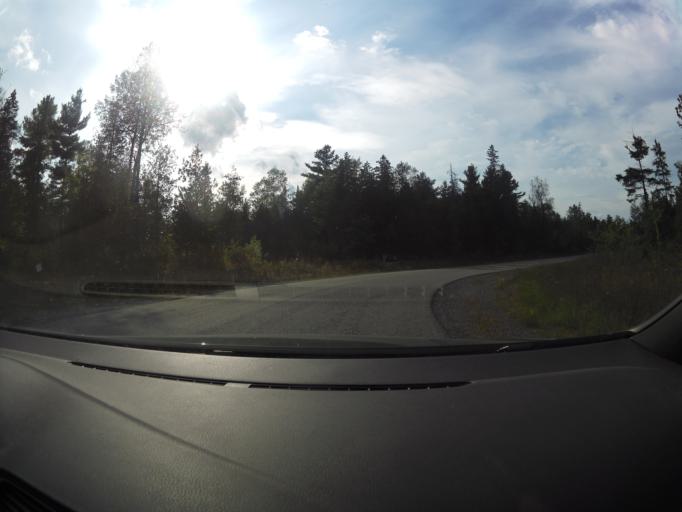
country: CA
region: Ontario
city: Carleton Place
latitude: 45.3360
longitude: -76.1609
